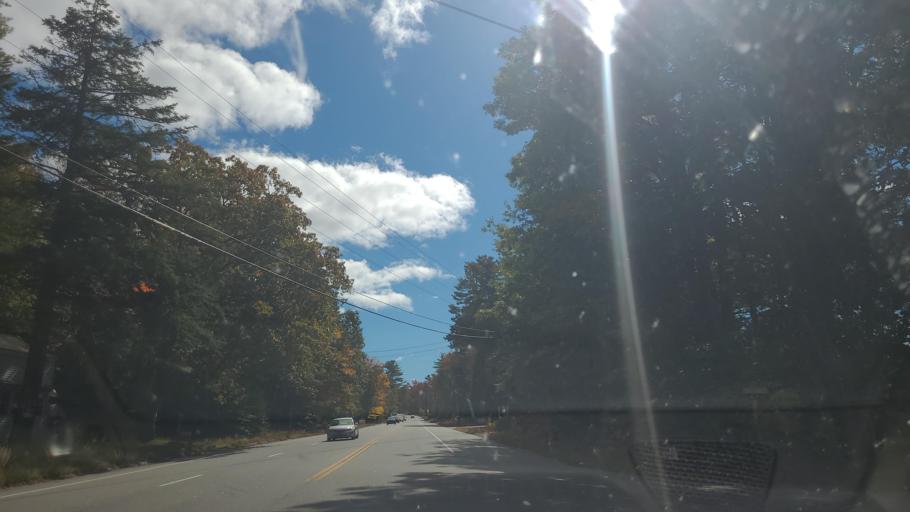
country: US
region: Maine
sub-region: Cumberland County
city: Raymond
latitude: 43.9325
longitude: -70.5395
